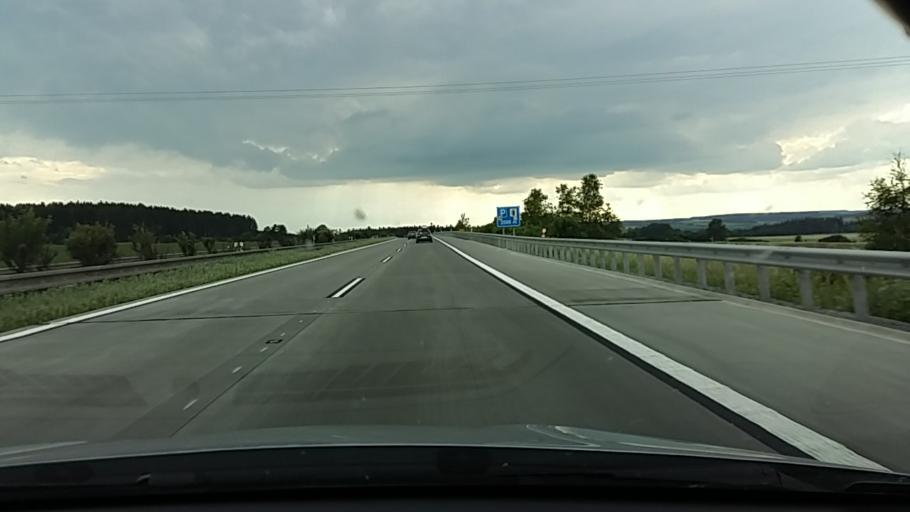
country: CZ
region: Plzensky
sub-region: Okres Tachov
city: Kladruby
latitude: 49.7071
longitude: 13.0212
